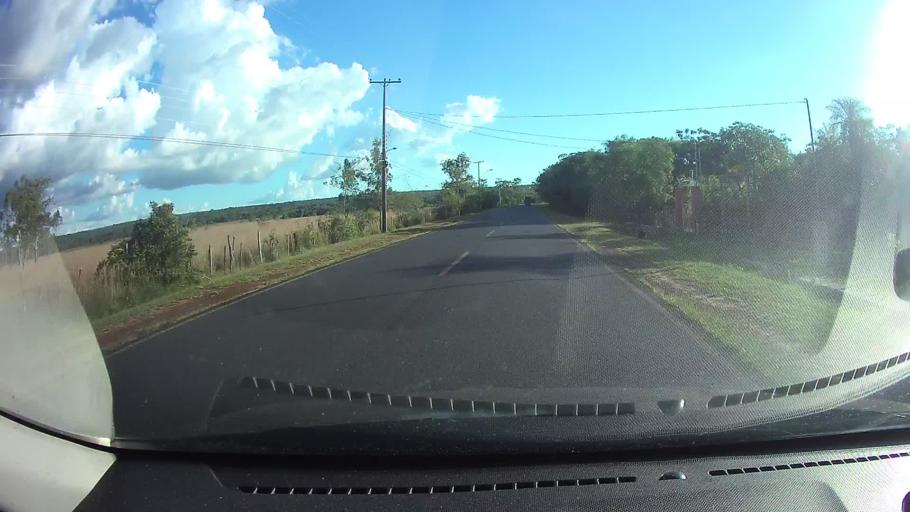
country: PY
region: Cordillera
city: Emboscada
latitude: -25.1589
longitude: -57.2637
